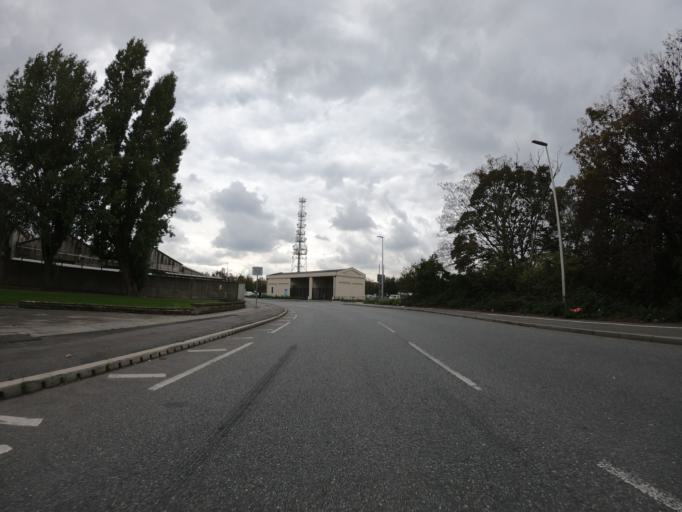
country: GB
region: England
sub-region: Greater London
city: Erith
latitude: 51.4936
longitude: 0.1673
